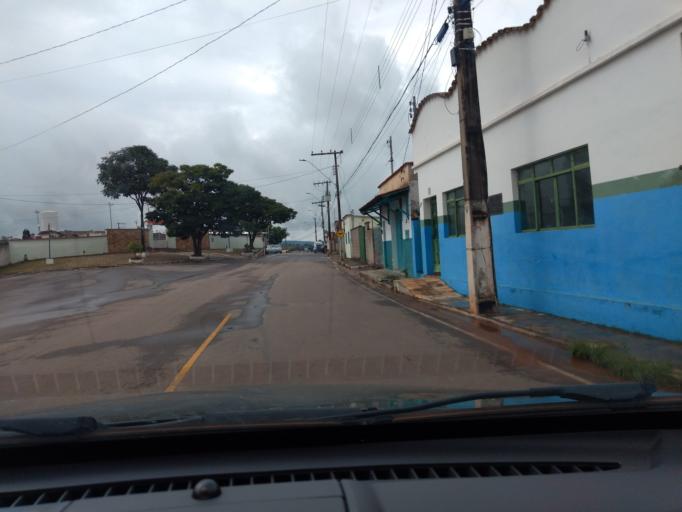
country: BR
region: Minas Gerais
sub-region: Lavras
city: Lavras
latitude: -21.5102
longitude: -44.9069
